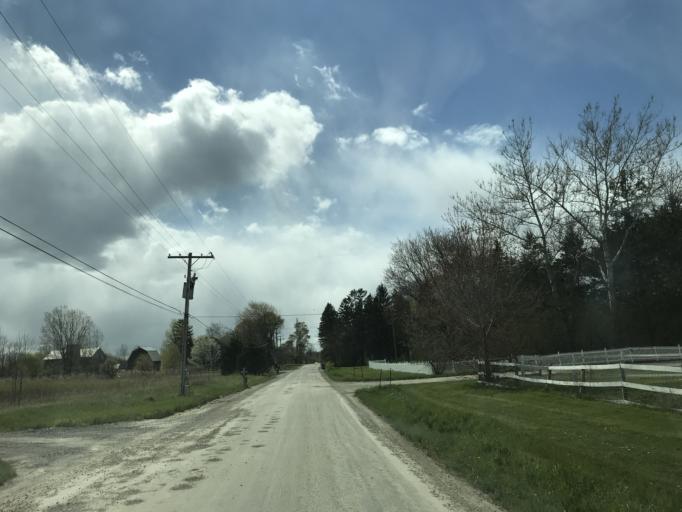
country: US
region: Michigan
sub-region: Oakland County
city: South Lyon
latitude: 42.3762
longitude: -83.6177
